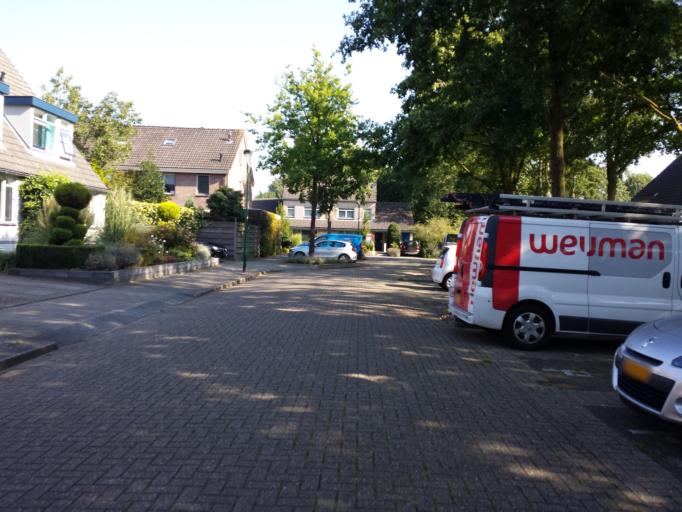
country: NL
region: Utrecht
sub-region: Gemeente Utrechtse Heuvelrug
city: Overberg
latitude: 52.0331
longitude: 5.5258
